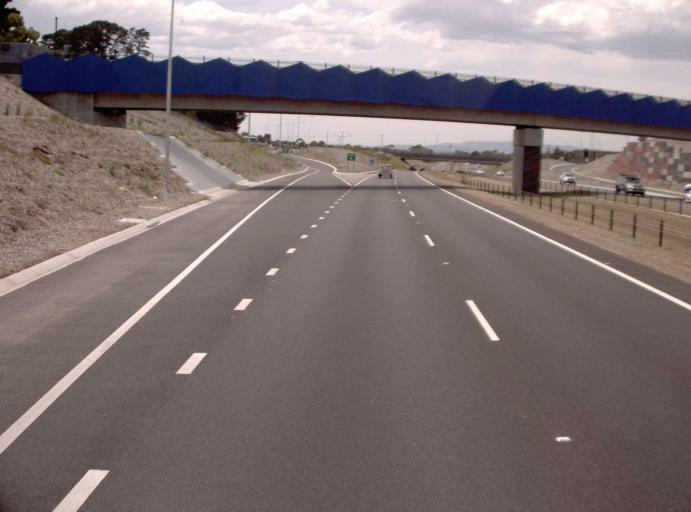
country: AU
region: Victoria
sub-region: Frankston
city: Langwarrin
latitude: -38.1600
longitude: 145.1663
